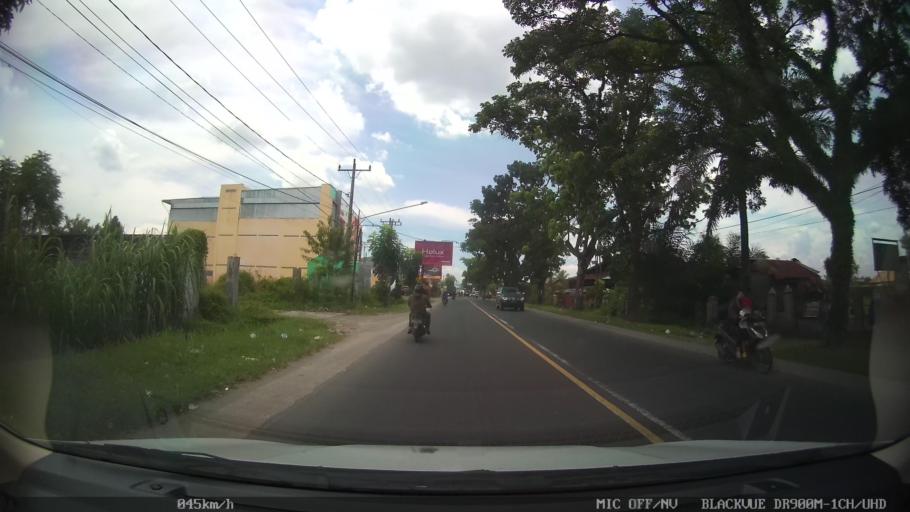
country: ID
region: North Sumatra
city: Binjai
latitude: 3.6224
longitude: 98.5036
